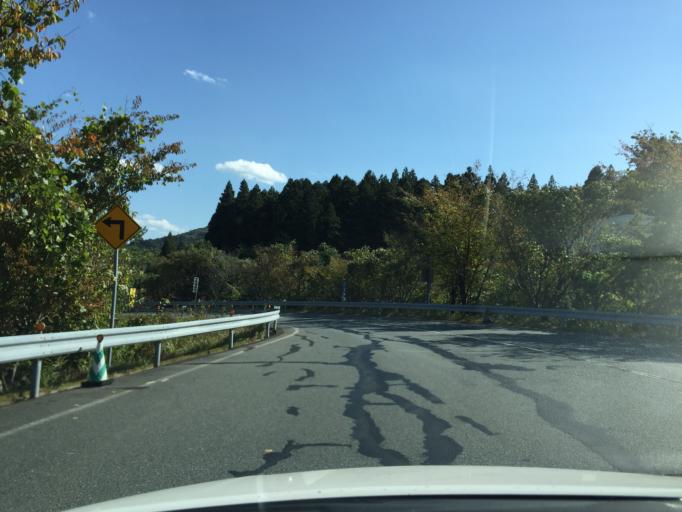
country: JP
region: Fukushima
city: Iwaki
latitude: 37.1013
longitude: 140.7716
